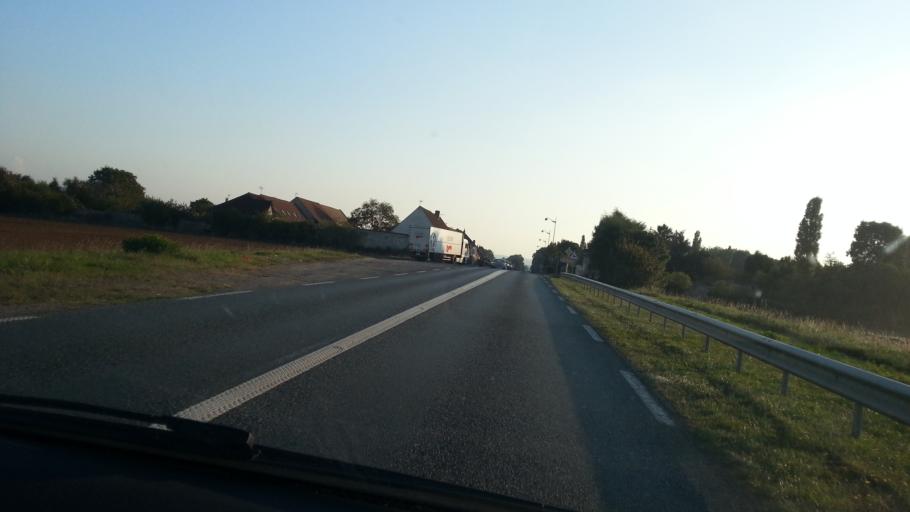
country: FR
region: Picardie
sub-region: Departement de l'Oise
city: Grandfresnoy
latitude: 49.3873
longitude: 2.6211
